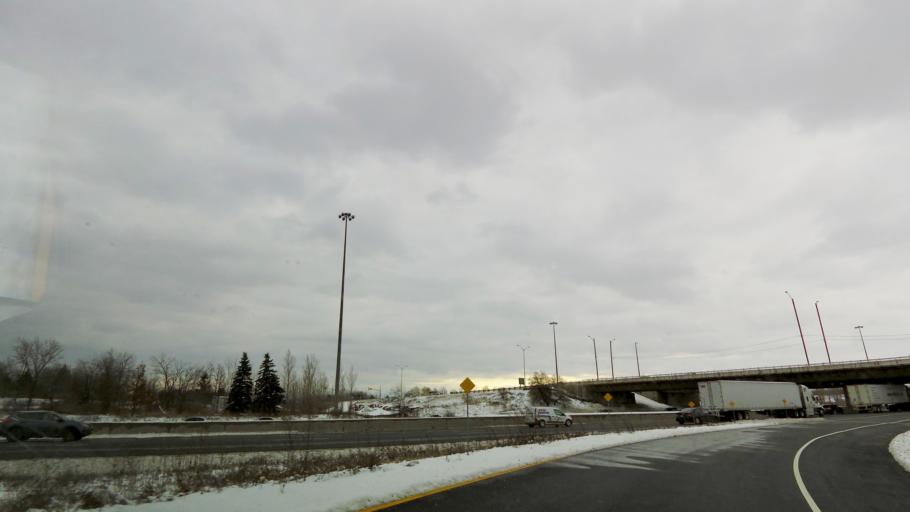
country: CA
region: Ontario
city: Mississauga
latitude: 43.5551
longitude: -79.6960
